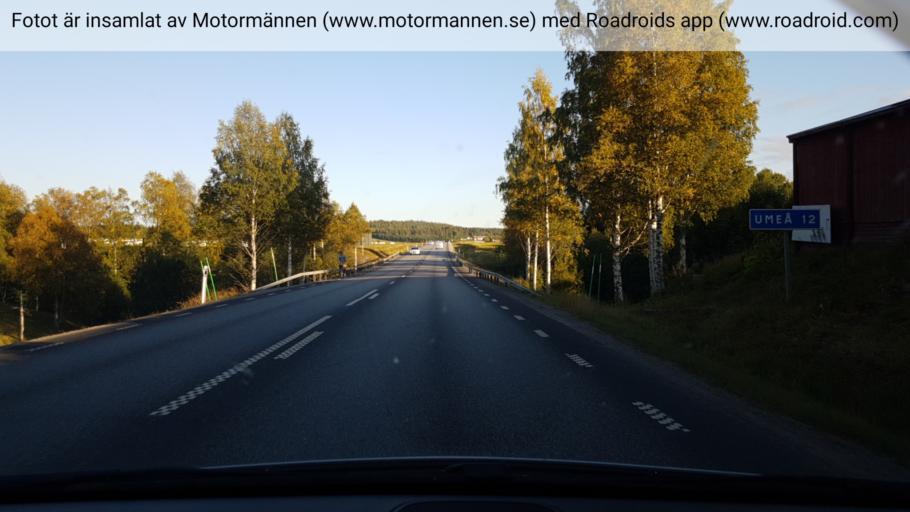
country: SE
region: Vaesterbotten
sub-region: Umea Kommun
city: Roback
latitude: 63.8735
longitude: 20.0664
